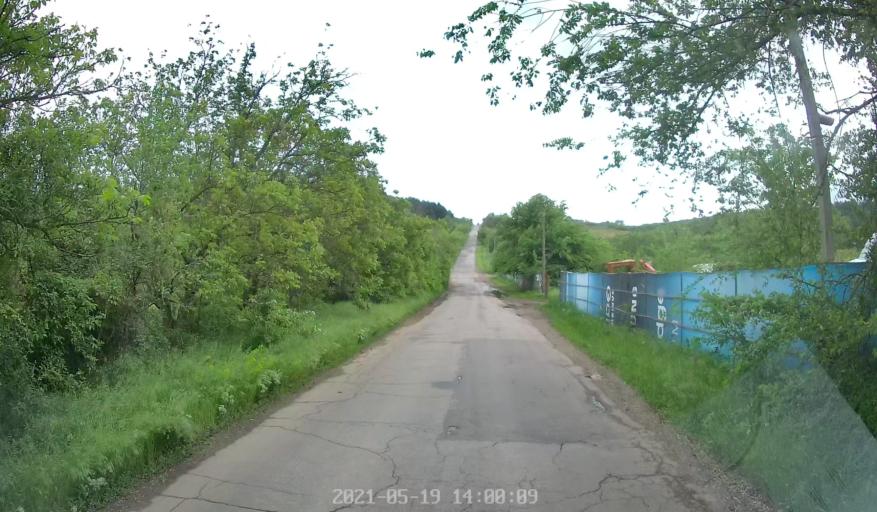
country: MD
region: Chisinau
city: Chisinau
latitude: 47.0364
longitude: 28.9298
